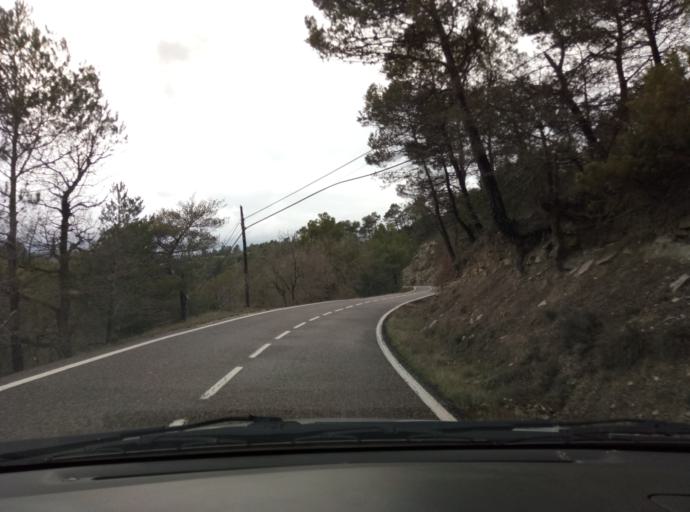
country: ES
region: Catalonia
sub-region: Provincia de Tarragona
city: Santa Coloma de Queralt
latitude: 41.5415
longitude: 1.3397
